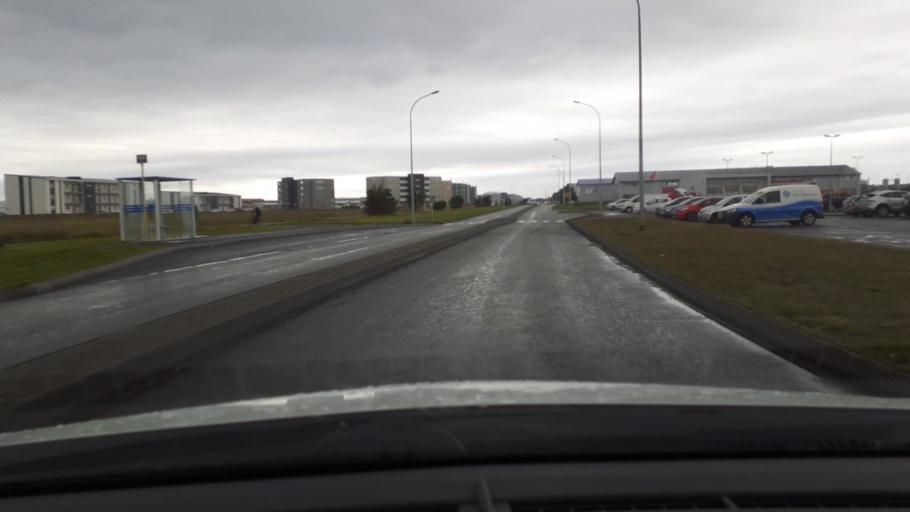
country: IS
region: West
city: Akranes
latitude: 64.3272
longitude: -22.0533
